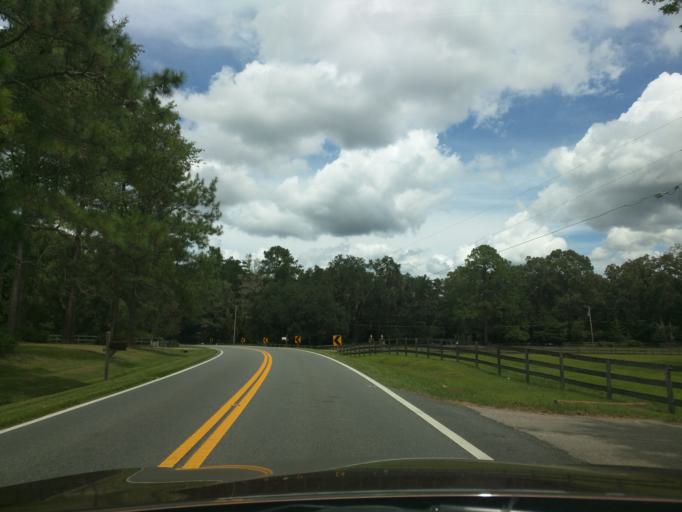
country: US
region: Florida
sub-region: Leon County
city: Tallahassee
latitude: 30.5561
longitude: -84.1764
